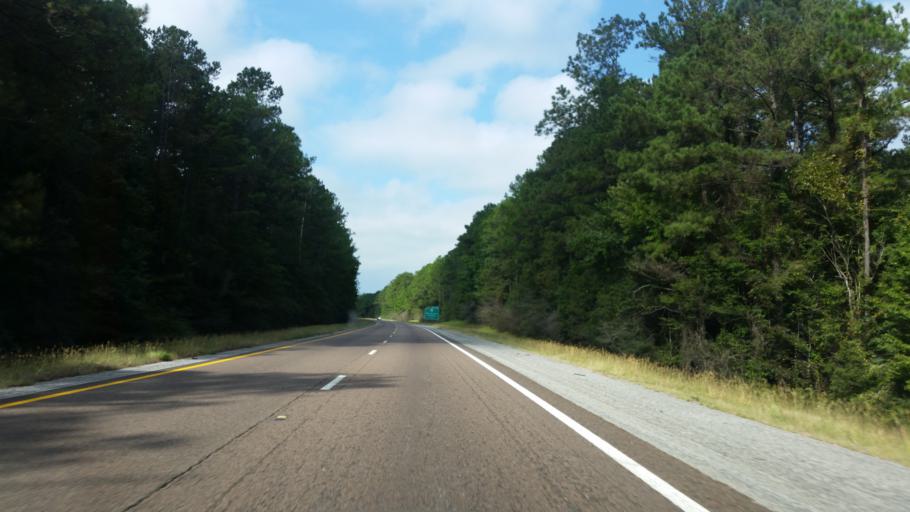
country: US
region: Alabama
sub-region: Baldwin County
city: Bay Minette
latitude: 30.9583
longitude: -87.8008
